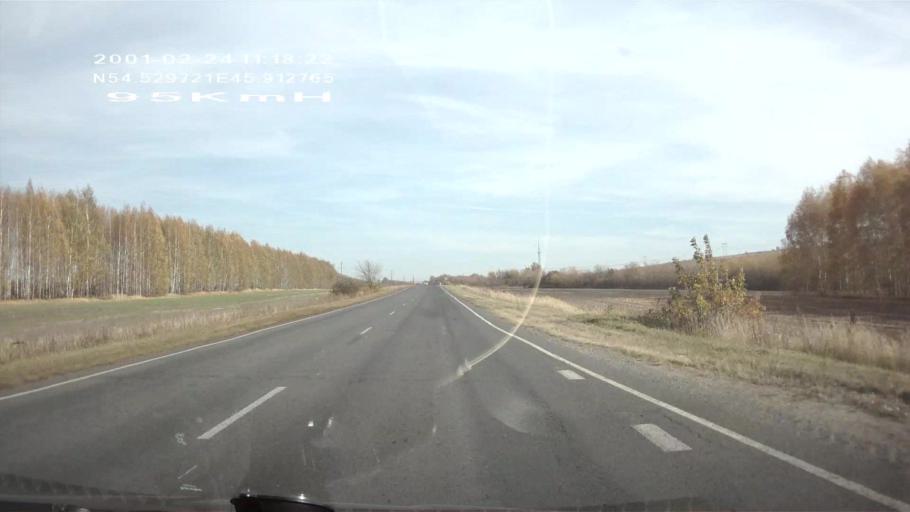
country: RU
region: Mordoviya
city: Atyashevo
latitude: 54.5296
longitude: 45.9126
